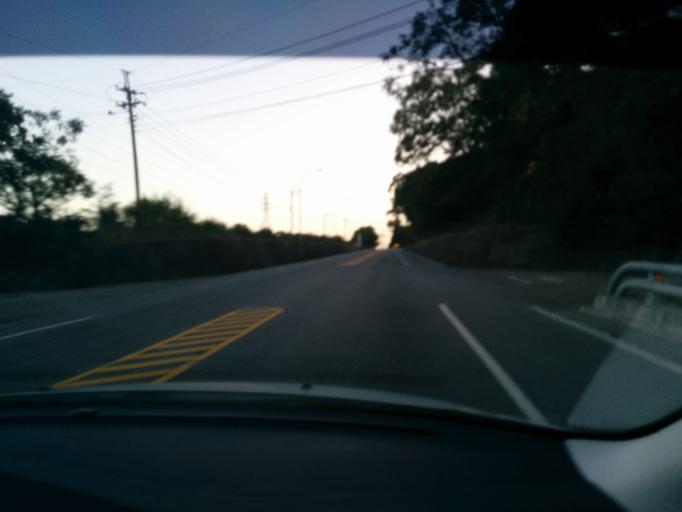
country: TW
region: Taiwan
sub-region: Taitung
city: Taitung
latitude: 22.9582
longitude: 121.1296
